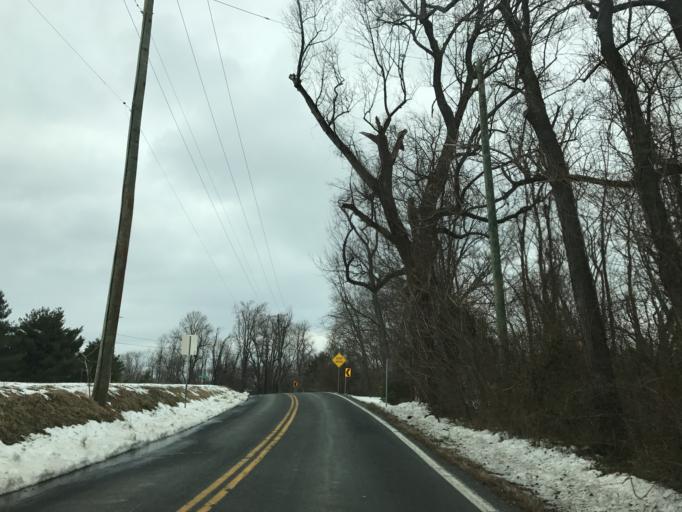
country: US
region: Maryland
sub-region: Harford County
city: Bel Air North
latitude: 39.5739
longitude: -76.4001
